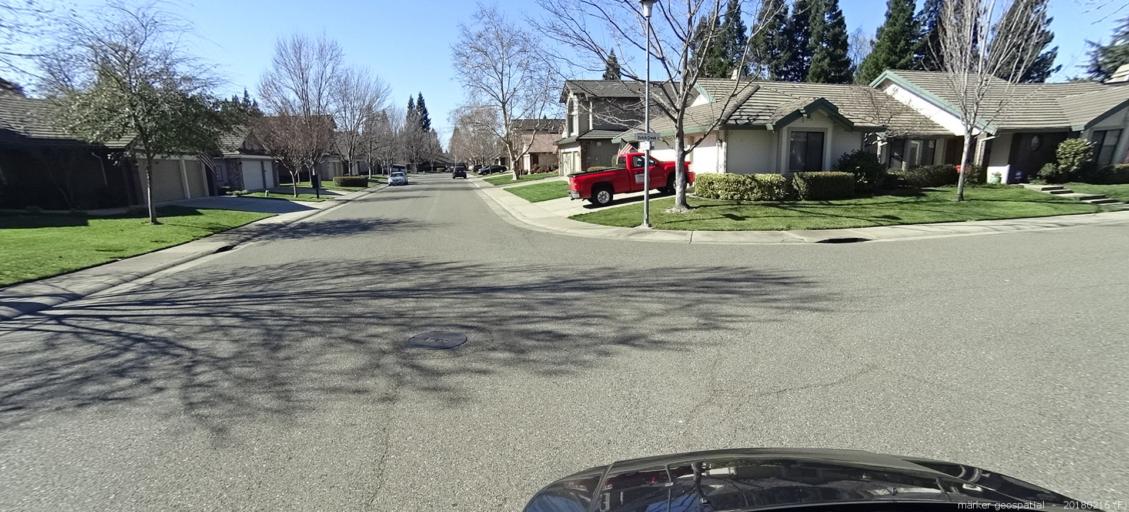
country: US
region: California
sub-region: Sacramento County
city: Gold River
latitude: 38.6230
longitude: -121.2356
